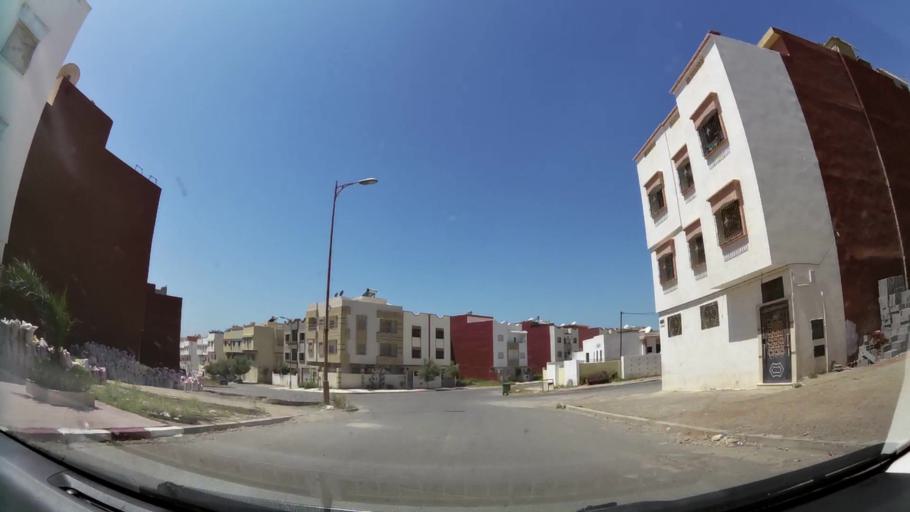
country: MA
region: Oued ed Dahab-Lagouira
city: Dakhla
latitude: 30.4300
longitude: -9.5586
